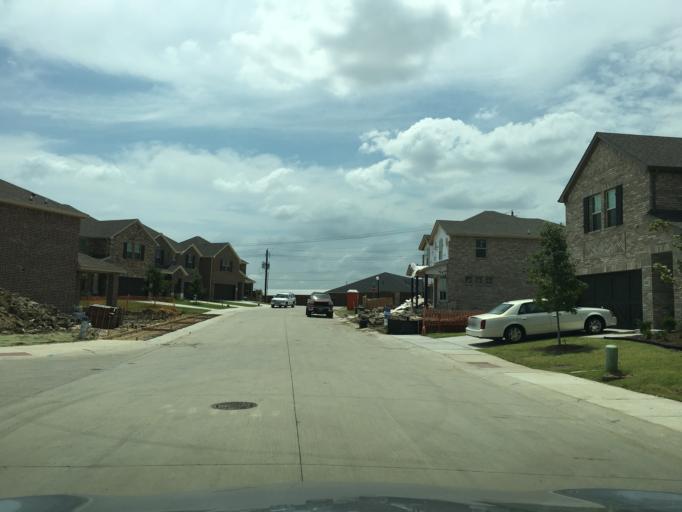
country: US
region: Texas
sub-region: Denton County
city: The Colony
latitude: 33.0428
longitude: -96.8619
